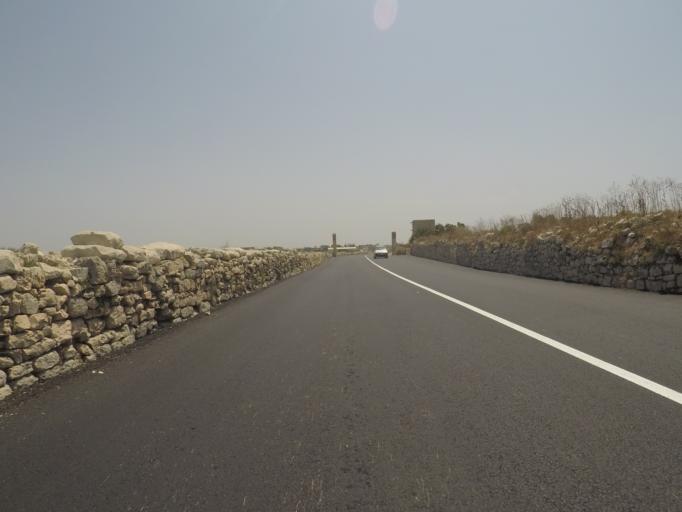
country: MT
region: L-Imdina
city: Imdina
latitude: 35.8791
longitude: 14.4107
